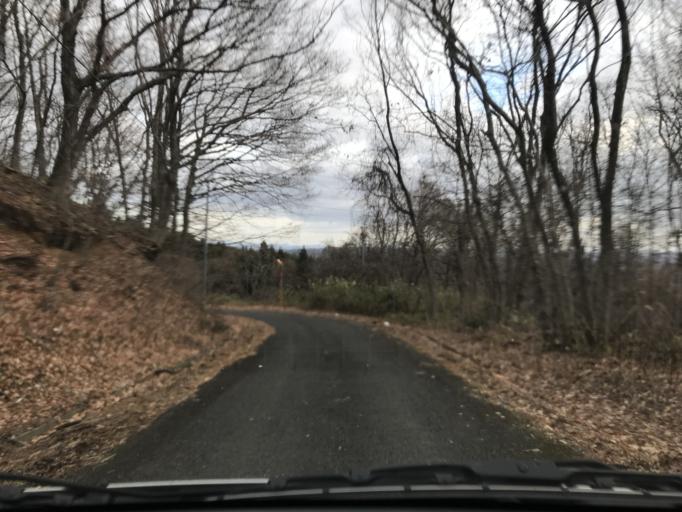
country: JP
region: Iwate
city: Ichinoseki
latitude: 38.9772
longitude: 141.0373
